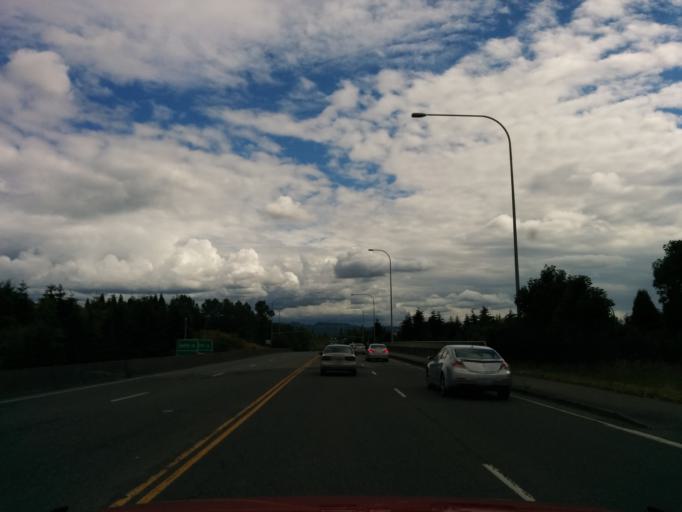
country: US
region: Washington
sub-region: King County
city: Redmond
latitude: 47.6353
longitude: -122.1431
